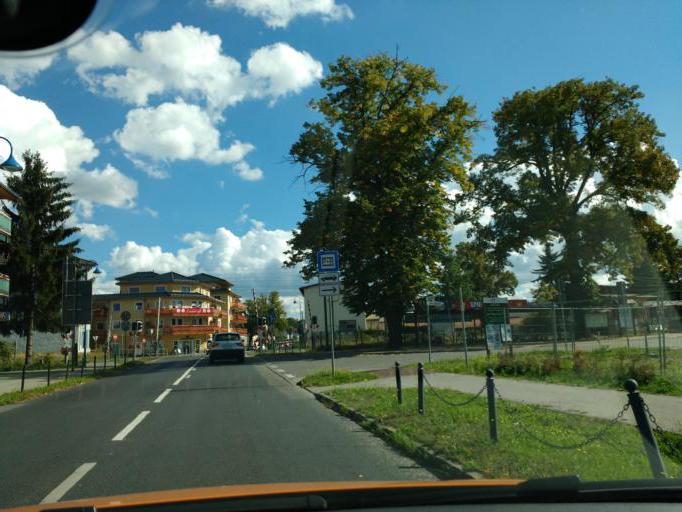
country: DE
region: Brandenburg
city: Bestensee
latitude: 52.2427
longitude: 13.6340
